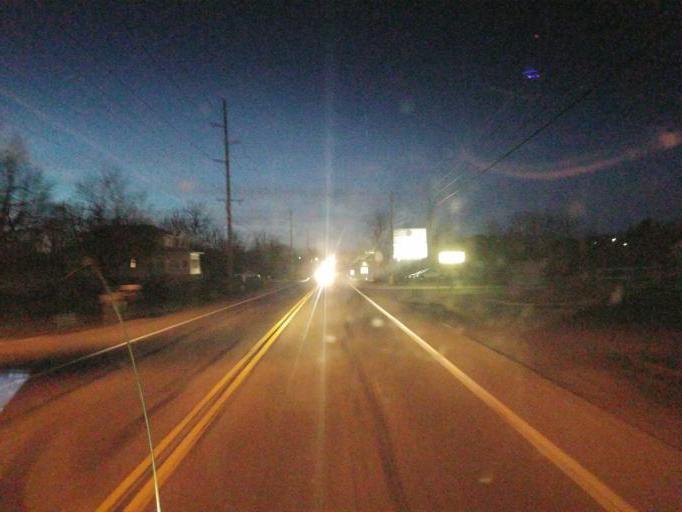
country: US
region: Ohio
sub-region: Logan County
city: Bellefontaine
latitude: 40.3873
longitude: -83.7525
